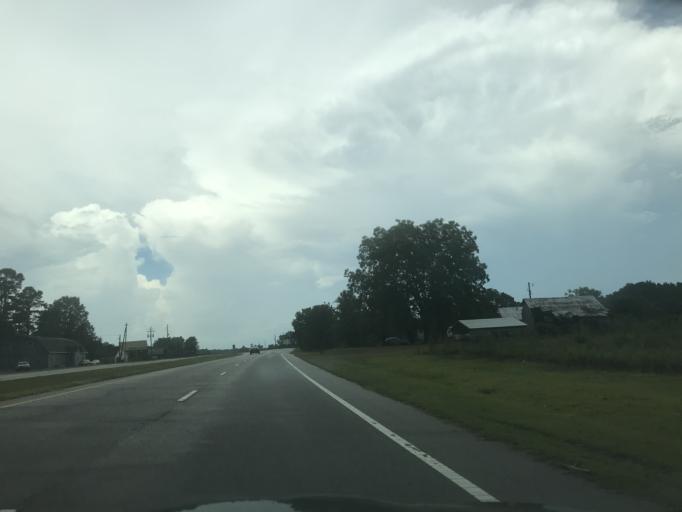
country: US
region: North Carolina
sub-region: Johnston County
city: Wilsons Mills
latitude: 35.5903
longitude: -78.4081
